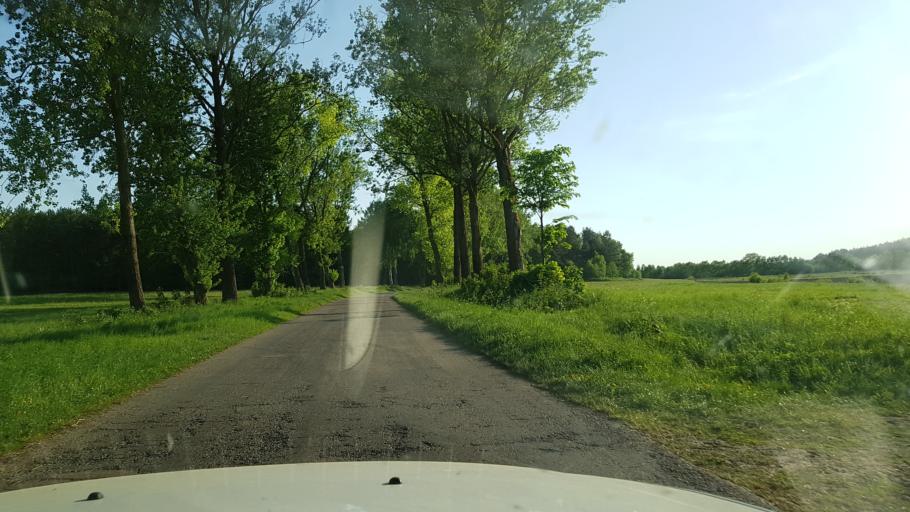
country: PL
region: West Pomeranian Voivodeship
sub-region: Powiat lobeski
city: Dobra
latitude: 53.6232
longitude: 15.3507
